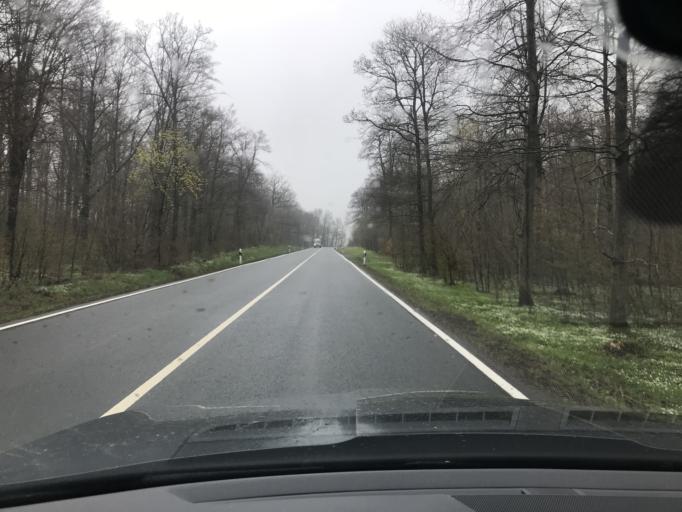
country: DE
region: Saxony-Anhalt
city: Harzgerode
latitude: 51.6219
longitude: 11.1531
